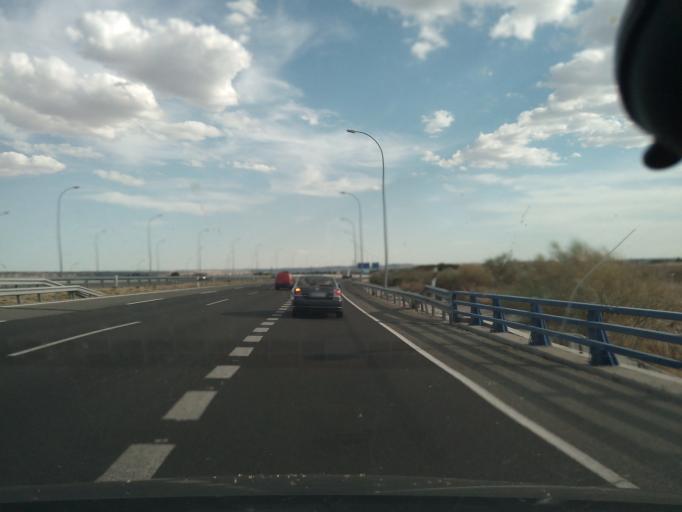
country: ES
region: Madrid
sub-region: Provincia de Madrid
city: Torrejon de Ardoz
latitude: 40.4803
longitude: -3.4962
